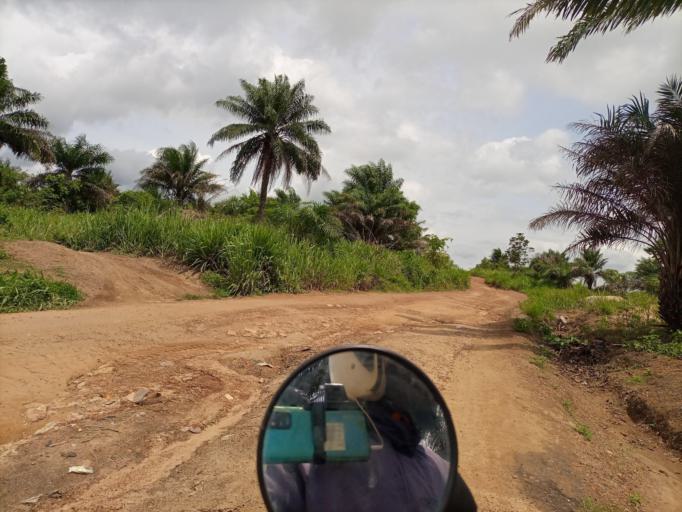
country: SL
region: Southern Province
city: Bo
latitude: 7.9780
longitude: -11.7721
